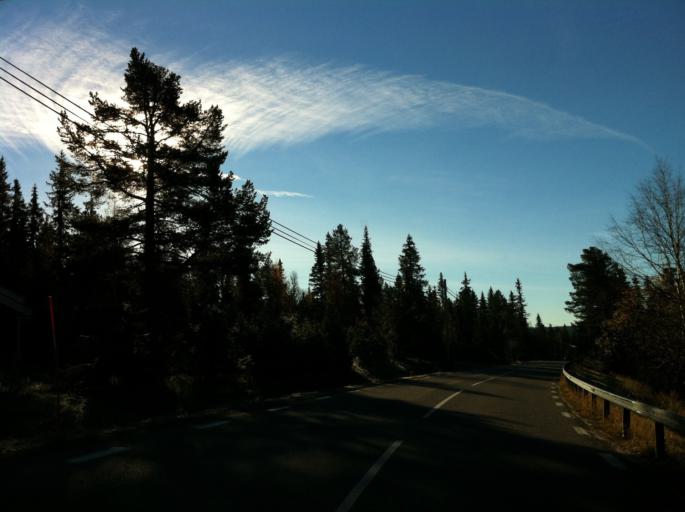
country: NO
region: Hedmark
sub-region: Engerdal
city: Engerdal
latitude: 62.0775
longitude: 12.3103
